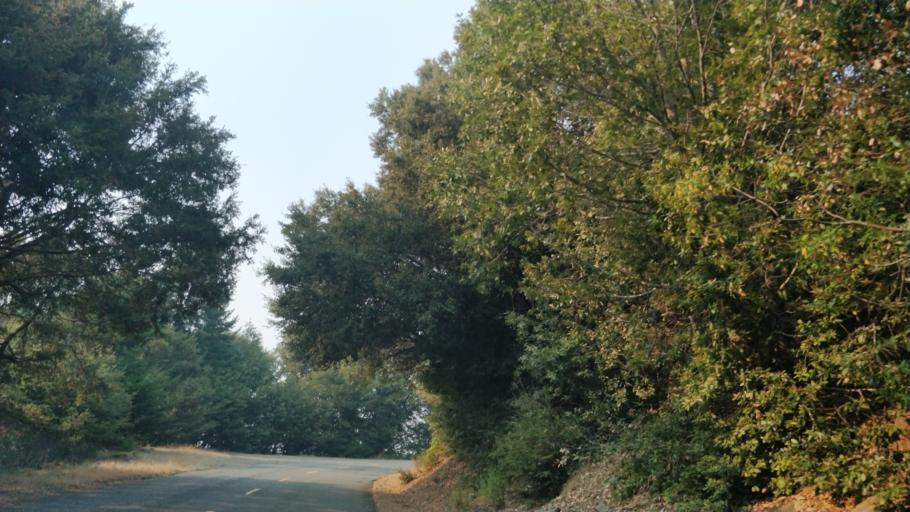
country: US
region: California
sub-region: Humboldt County
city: Rio Dell
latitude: 40.2601
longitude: -124.1151
